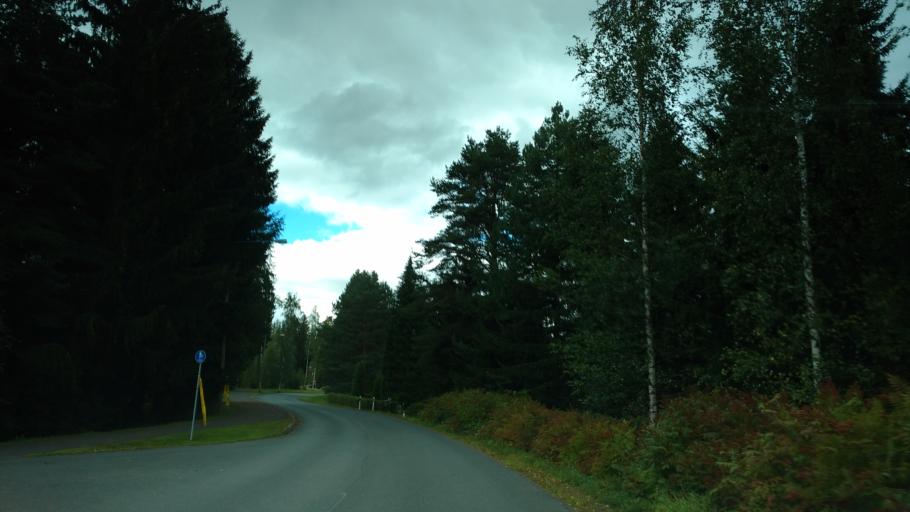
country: FI
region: Haeme
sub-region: Forssa
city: Ypaejae
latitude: 60.8076
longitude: 23.2651
